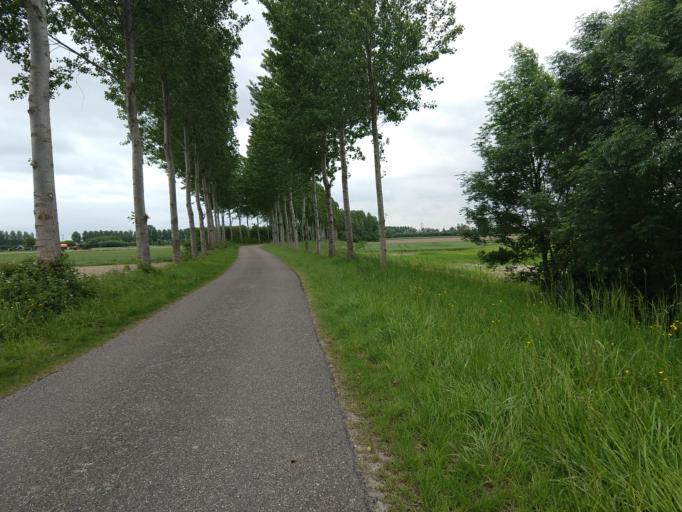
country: NL
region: Zeeland
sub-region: Gemeente Borsele
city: Borssele
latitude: 51.4580
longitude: 3.7954
